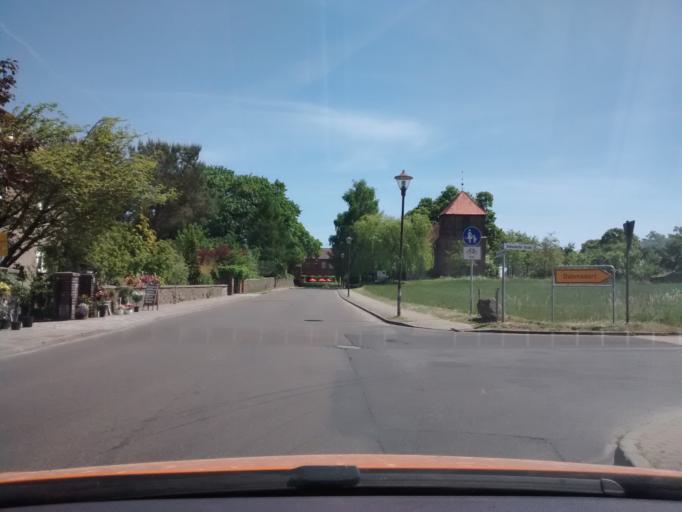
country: DE
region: Brandenburg
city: Reichenwalde
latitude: 52.2647
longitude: 13.9957
